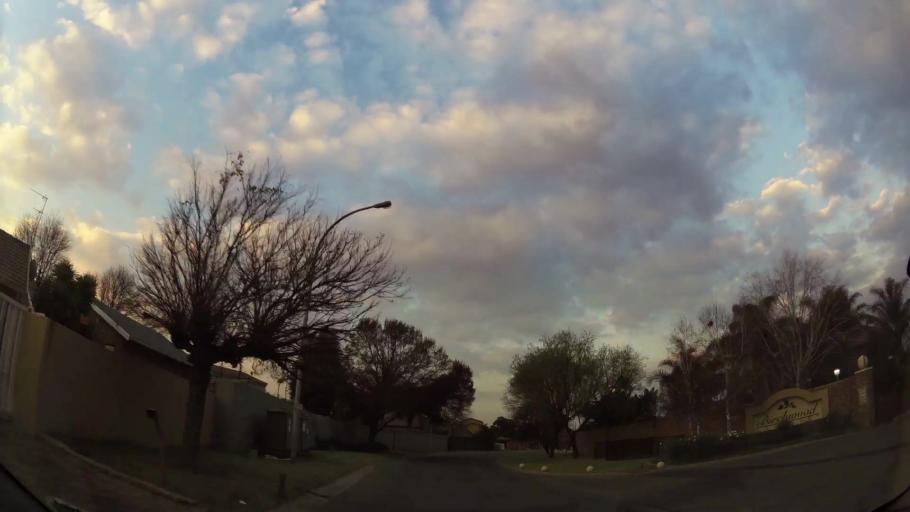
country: ZA
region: Gauteng
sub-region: Ekurhuleni Metropolitan Municipality
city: Benoni
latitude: -26.1720
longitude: 28.3086
